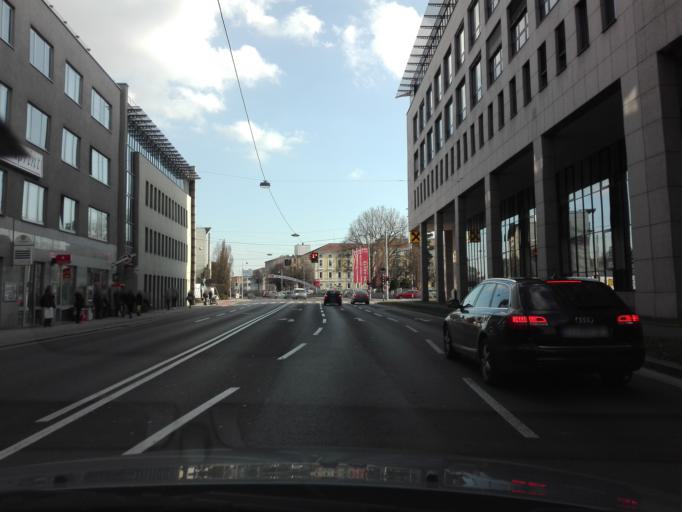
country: AT
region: Upper Austria
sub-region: Linz Stadt
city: Linz
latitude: 48.2997
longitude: 14.3025
